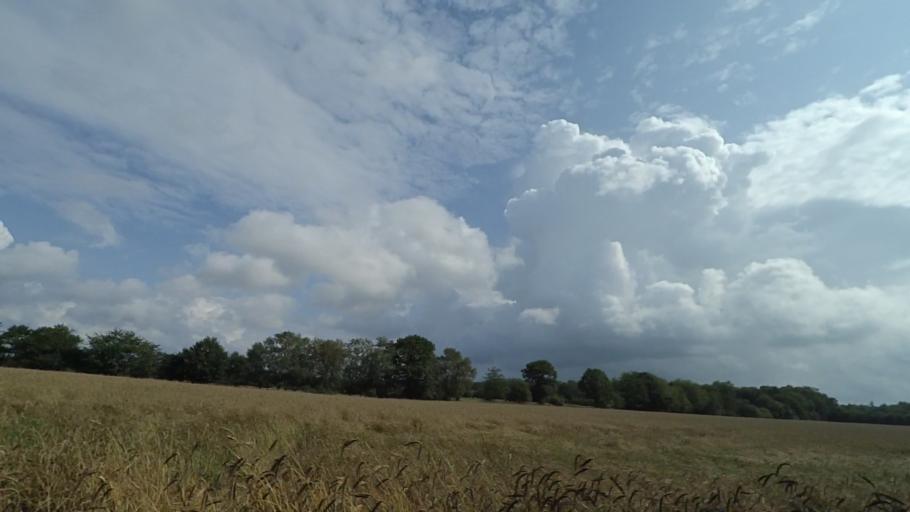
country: DK
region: Central Jutland
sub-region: Syddjurs Kommune
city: Ryomgard
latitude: 56.4640
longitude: 10.5237
